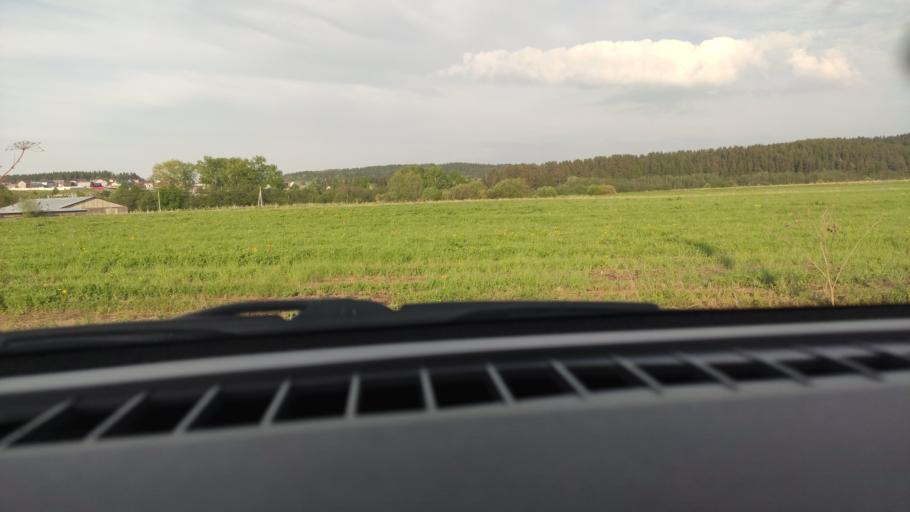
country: RU
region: Perm
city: Kultayevo
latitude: 57.8942
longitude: 55.9913
